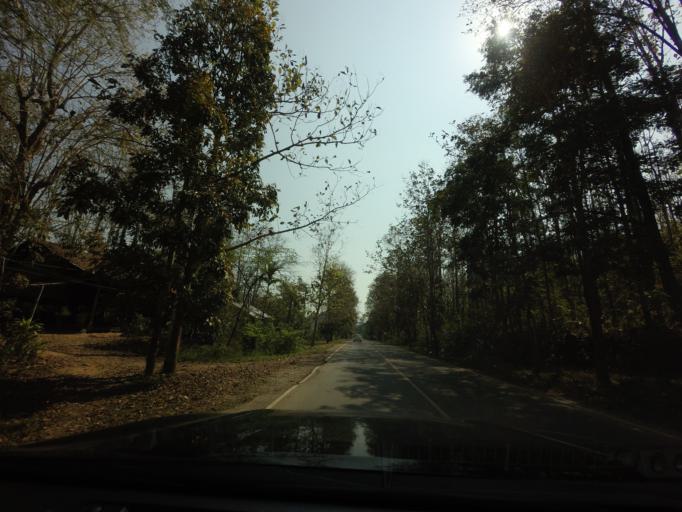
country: TH
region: Kanchanaburi
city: Thong Pha Phum
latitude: 14.6572
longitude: 98.5370
